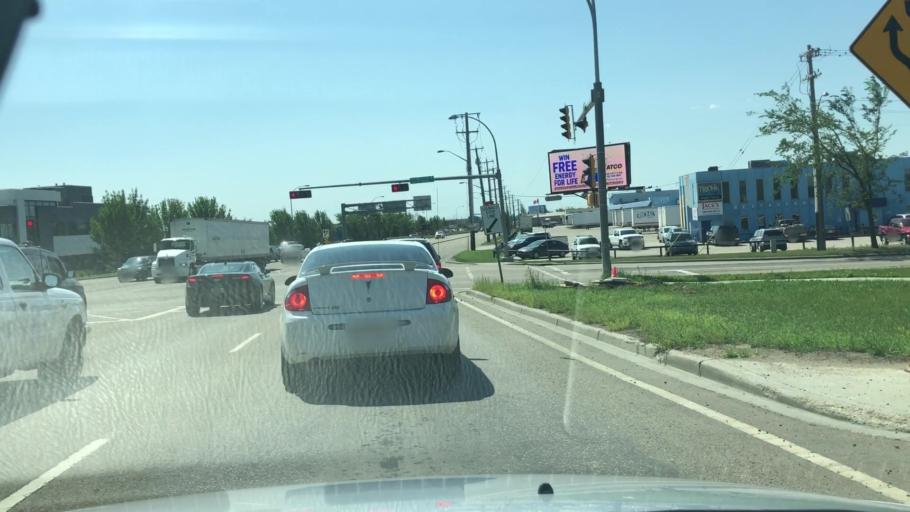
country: CA
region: Alberta
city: St. Albert
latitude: 53.5780
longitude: -113.5906
